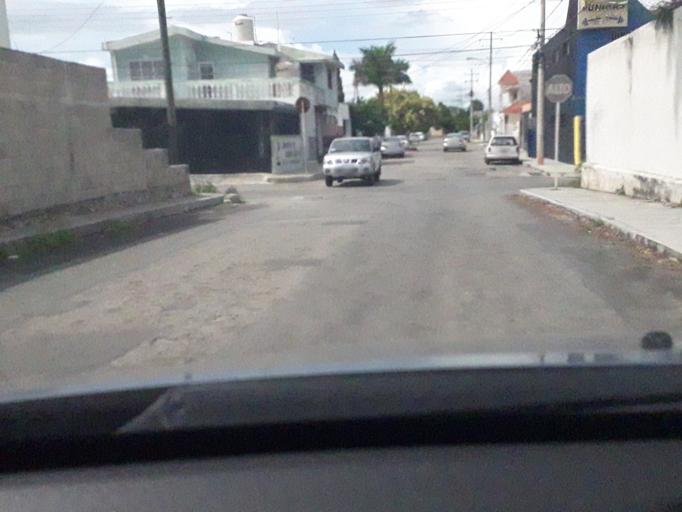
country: MX
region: Yucatan
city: Merida
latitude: 20.9808
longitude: -89.6572
